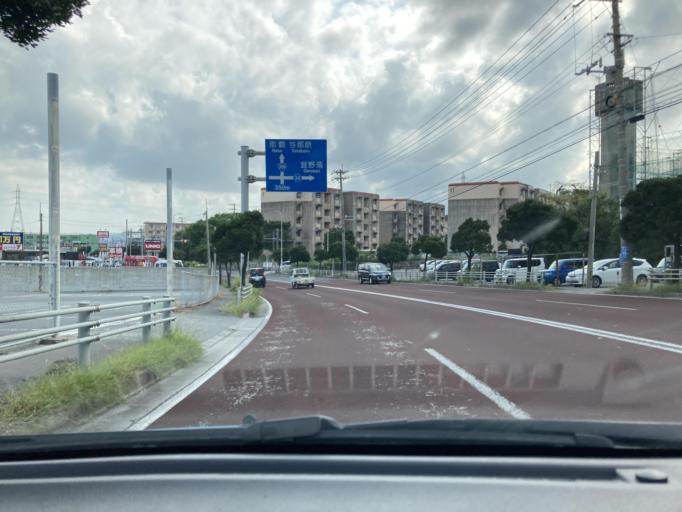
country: JP
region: Okinawa
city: Ginowan
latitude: 26.2362
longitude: 127.7698
